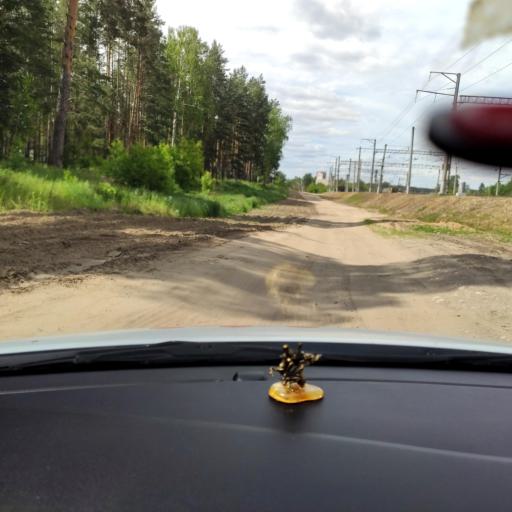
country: RU
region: Tatarstan
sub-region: Zelenodol'skiy Rayon
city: Vasil'yevo
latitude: 55.8408
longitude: 48.7243
